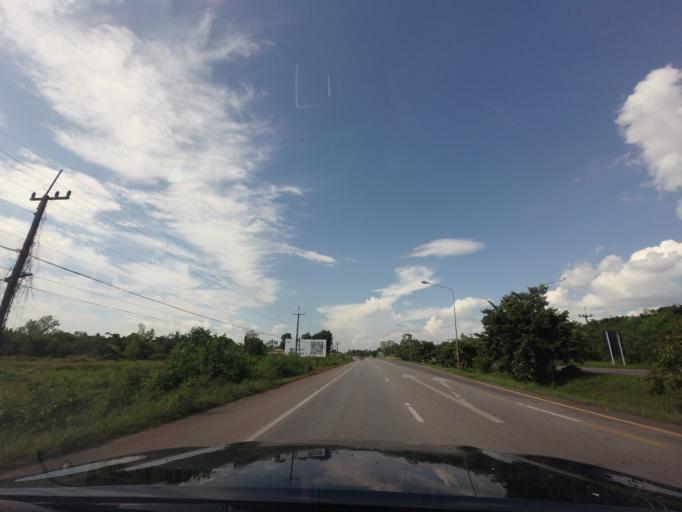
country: TH
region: Nong Khai
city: Sa Khrai
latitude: 17.6690
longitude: 102.7907
